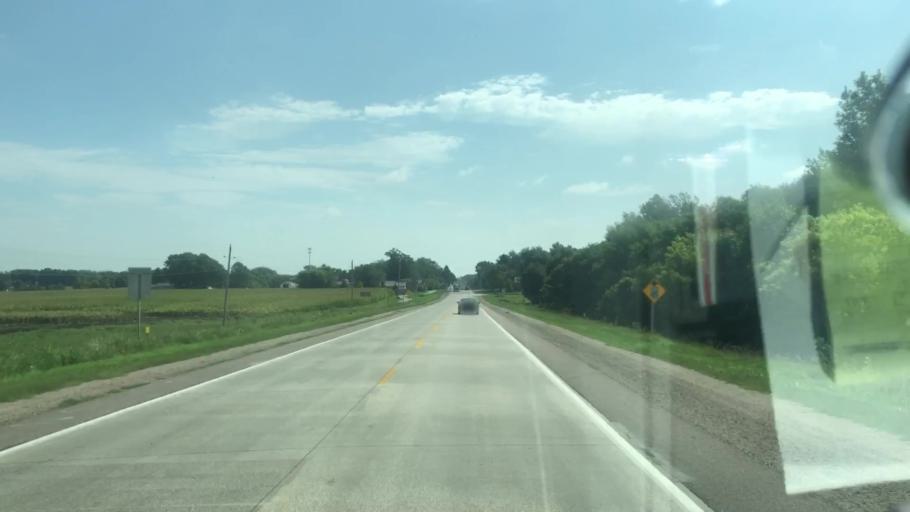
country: US
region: Iowa
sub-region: O'Brien County
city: Sheldon
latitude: 43.1858
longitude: -95.8672
